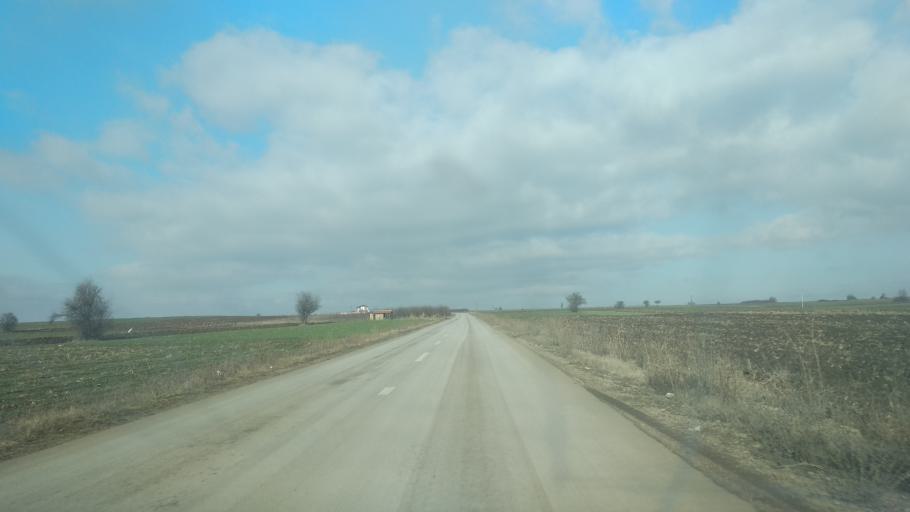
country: XK
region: Pristina
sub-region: Lipjan
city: Lipljan
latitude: 42.5531
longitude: 21.1771
